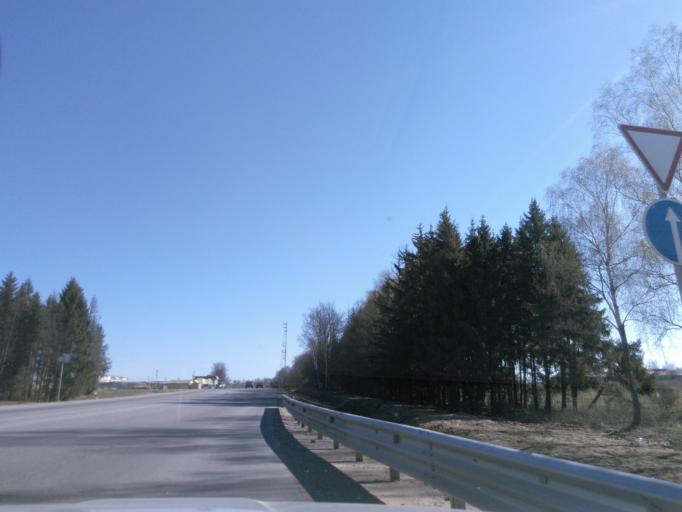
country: RU
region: Moskovskaya
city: Radumlya
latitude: 56.1007
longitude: 37.1793
